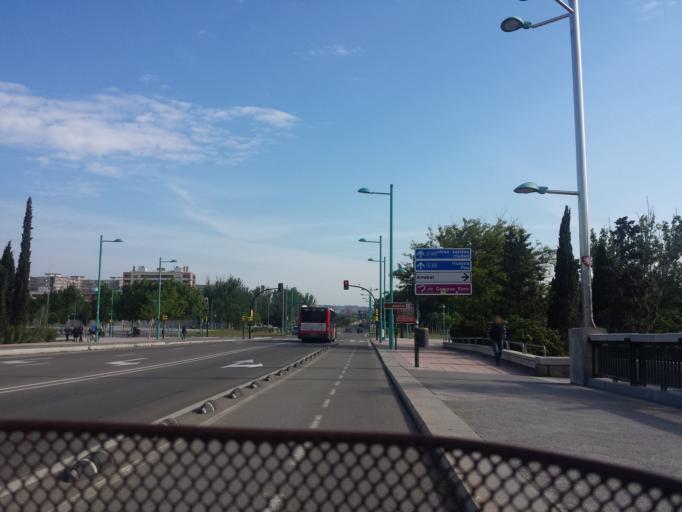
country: ES
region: Aragon
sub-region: Provincia de Zaragoza
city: Zaragoza
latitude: 41.6595
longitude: -0.8813
